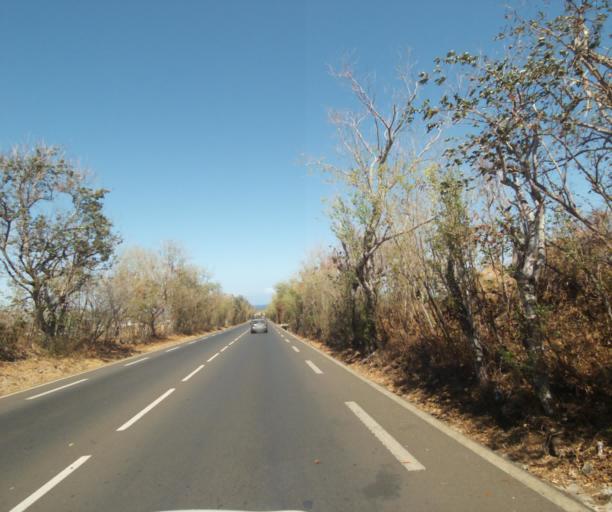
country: RE
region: Reunion
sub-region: Reunion
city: Saint-Paul
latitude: -20.9819
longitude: 55.3089
